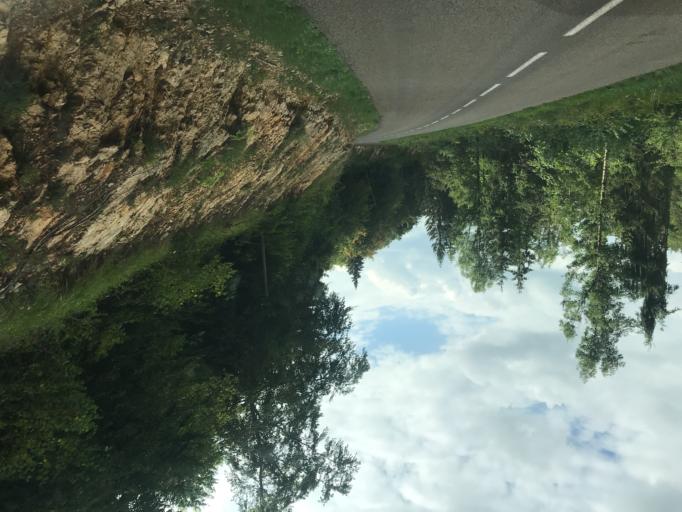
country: FR
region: Franche-Comte
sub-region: Departement du Jura
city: Valfin-les-Saint-Claude
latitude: 46.4667
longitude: 5.8347
